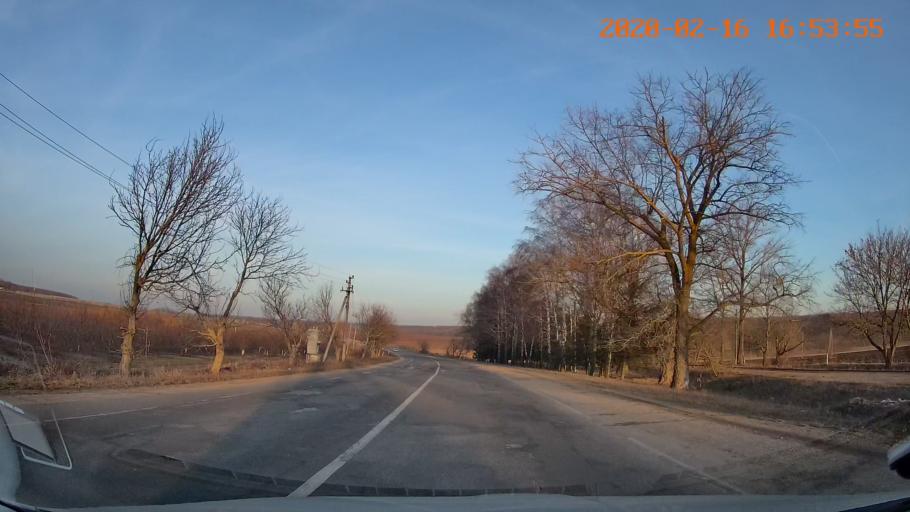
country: MD
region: Briceni
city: Briceni
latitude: 48.3163
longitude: 26.9961
